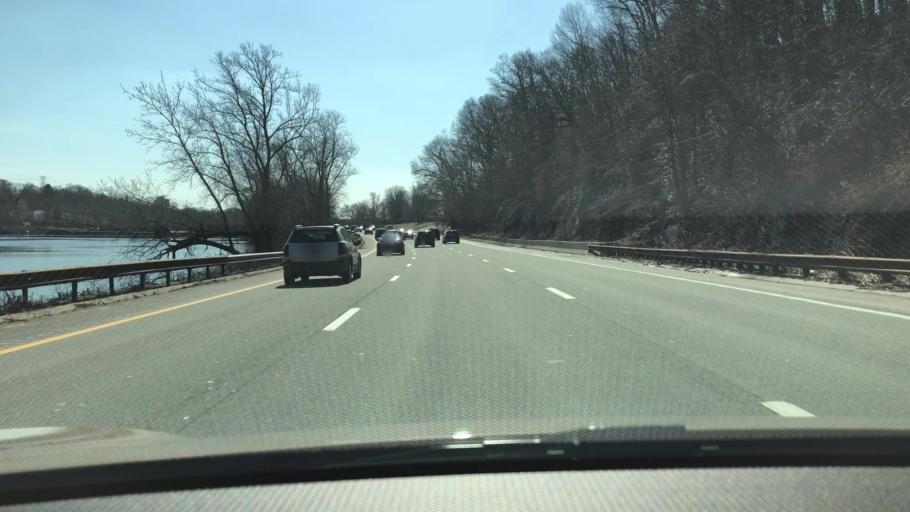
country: US
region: New York
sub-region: Westchester County
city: Tuckahoe
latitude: 40.9644
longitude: -73.8535
